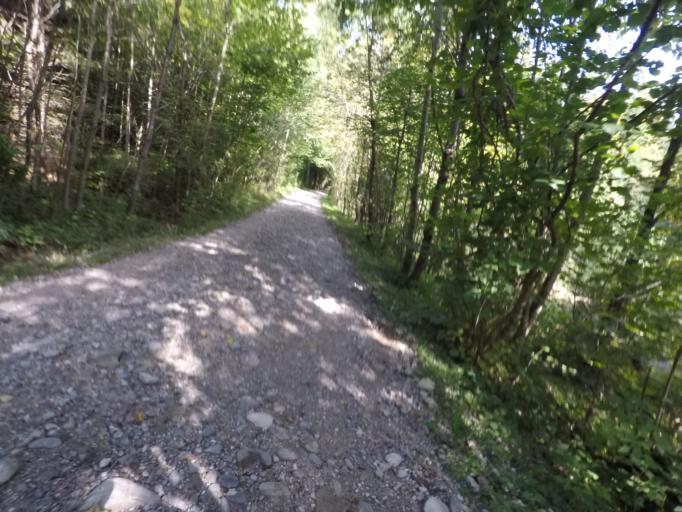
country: DE
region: Bavaria
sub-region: Upper Bavaria
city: Bad Toelz
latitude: 47.7949
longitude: 11.5676
